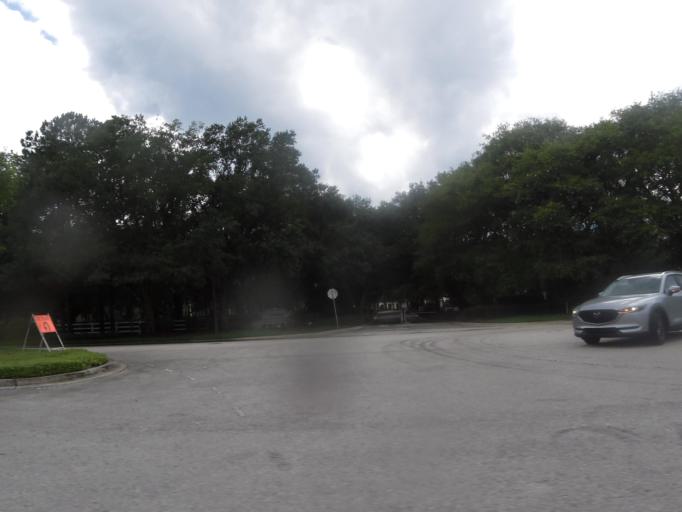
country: US
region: Florida
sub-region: Saint Johns County
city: Ponte Vedra Beach
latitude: 30.2542
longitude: -81.4369
